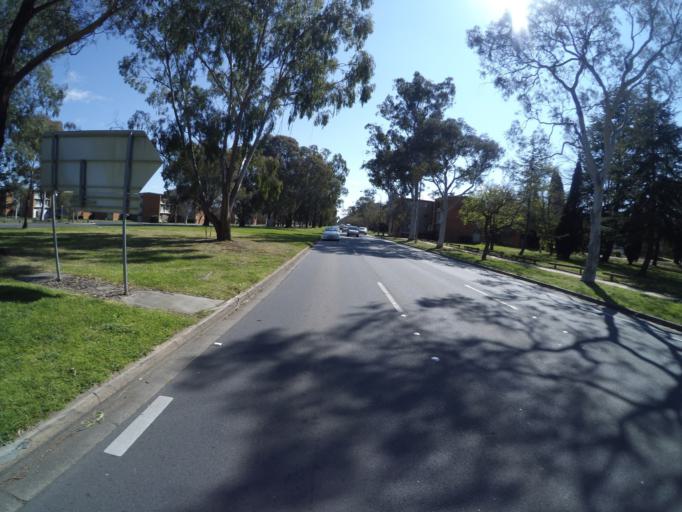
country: AU
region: Australian Capital Territory
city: Canberra
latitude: -35.2694
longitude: 149.1309
